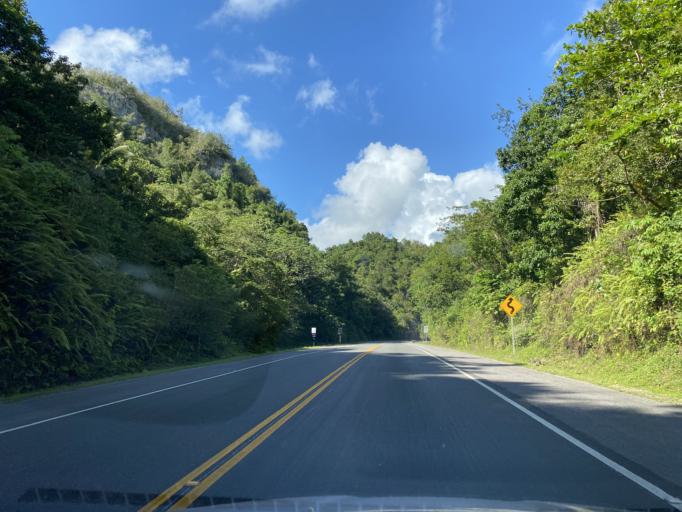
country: DO
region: Monte Plata
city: Majagual
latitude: 19.0724
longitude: -69.8297
